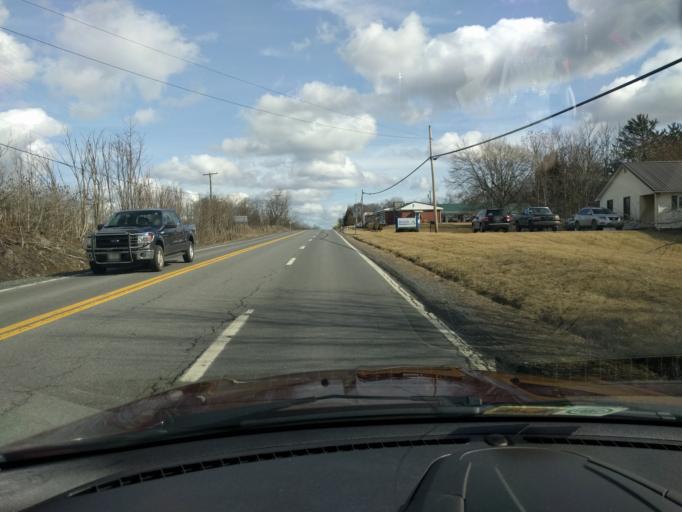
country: US
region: West Virginia
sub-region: Greenbrier County
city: Lewisburg
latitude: 37.8056
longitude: -80.4578
